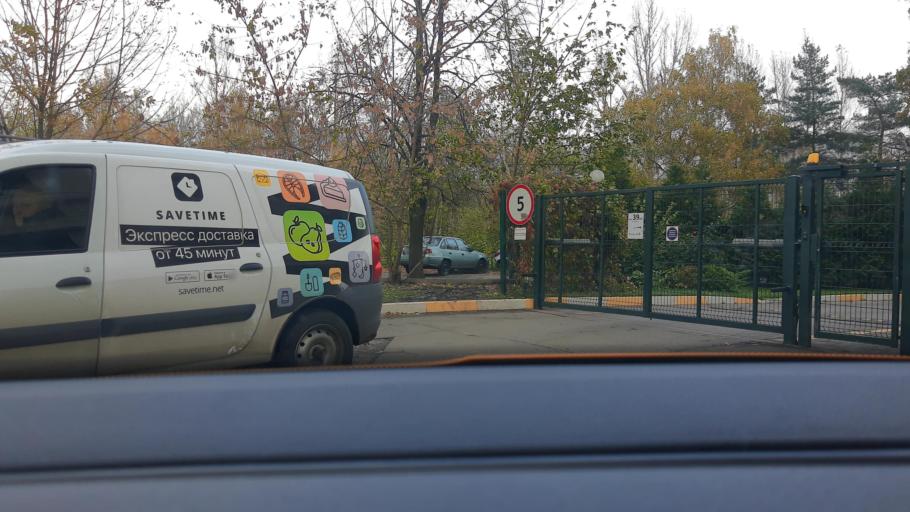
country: RU
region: Moscow
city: Strogino
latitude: 55.8069
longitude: 37.4229
